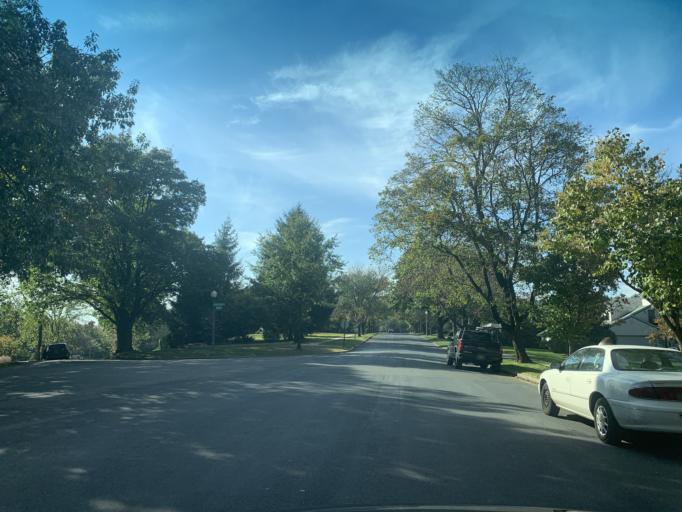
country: US
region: Pennsylvania
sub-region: Berks County
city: Wyomissing Hills
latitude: 40.3322
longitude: -75.9841
